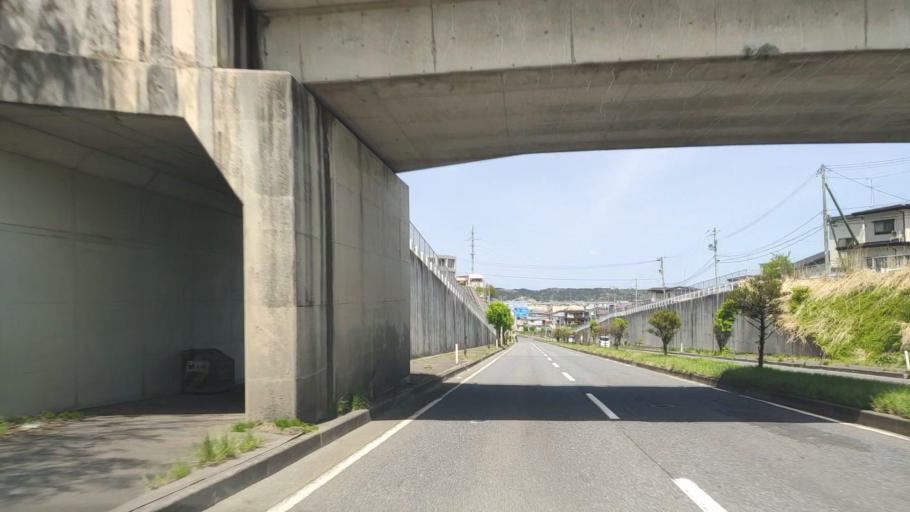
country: JP
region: Aomori
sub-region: Hachinohe Shi
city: Uchimaru
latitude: 40.4985
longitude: 141.4569
